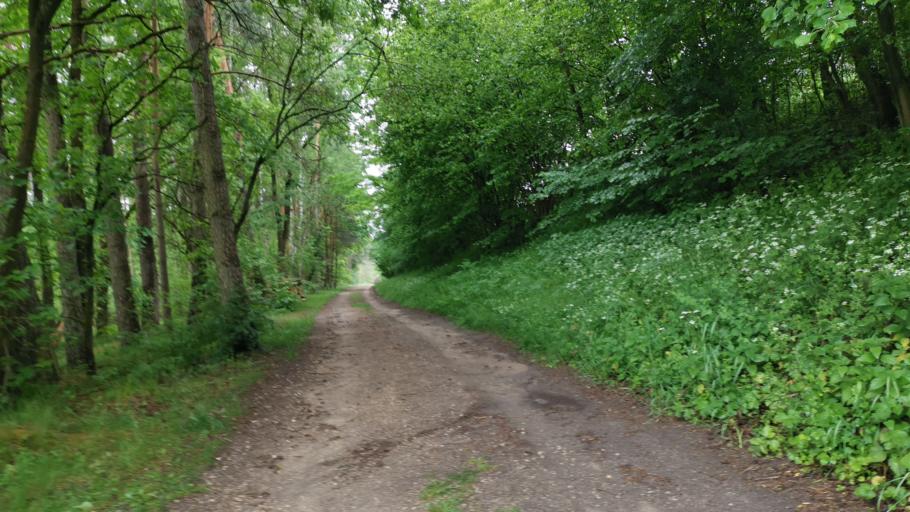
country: DE
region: Bavaria
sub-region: Regierungsbezirk Mittelfranken
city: Roth
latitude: 49.2567
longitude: 11.1101
